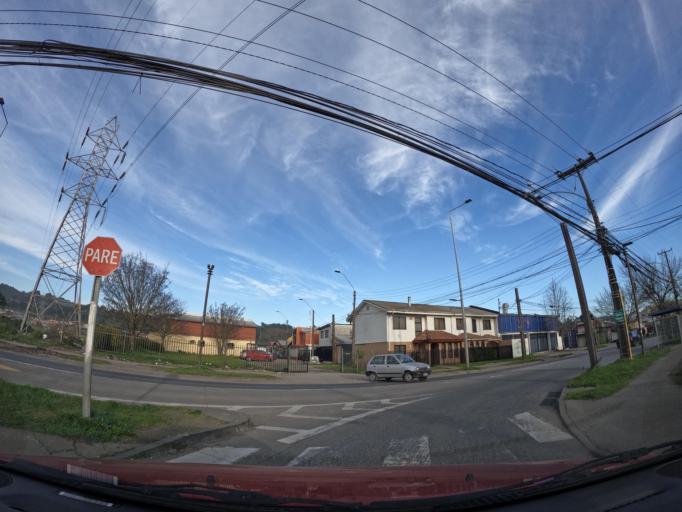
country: CL
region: Biobio
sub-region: Provincia de Concepcion
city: Concepcion
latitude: -36.8032
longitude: -73.0300
